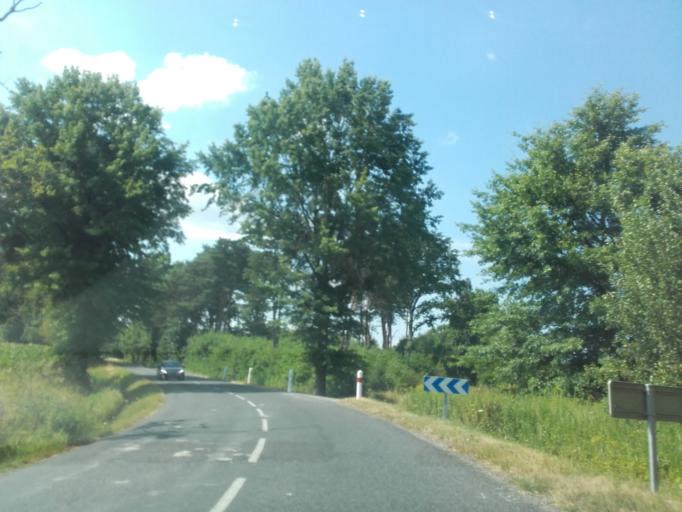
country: FR
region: Rhone-Alpes
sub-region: Departement de l'Ain
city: Chalamont
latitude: 46.0250
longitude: 5.1293
